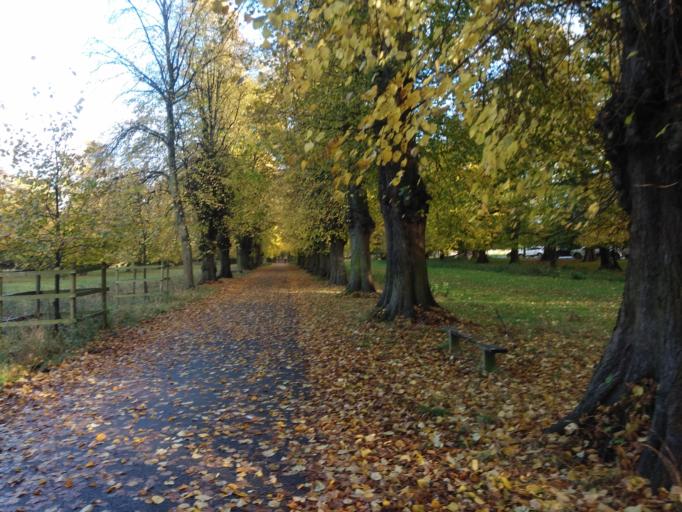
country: GB
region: England
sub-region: Nottingham
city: Nottingham
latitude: 52.9473
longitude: -1.1984
